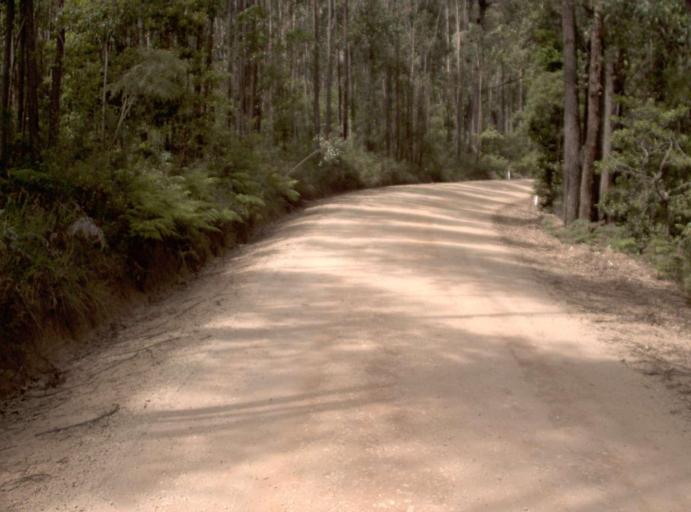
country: AU
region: Victoria
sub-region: East Gippsland
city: Lakes Entrance
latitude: -37.6201
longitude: 148.6840
